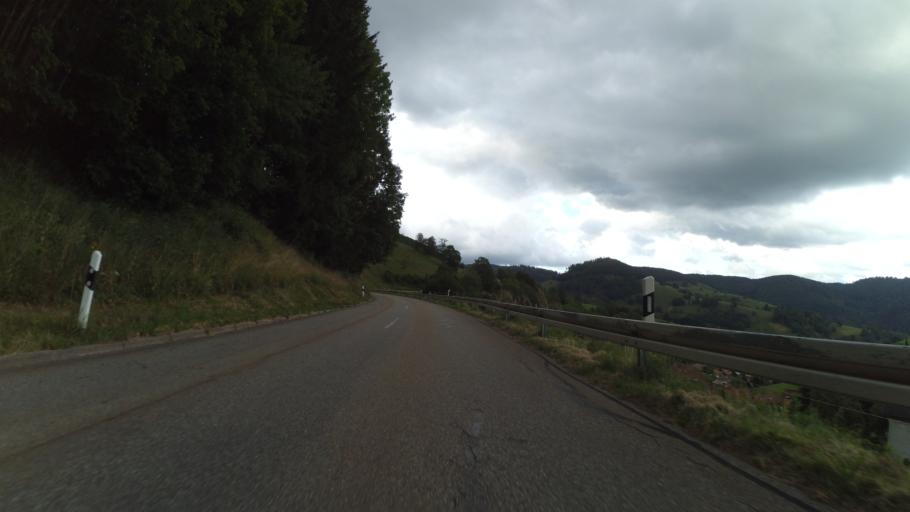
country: DE
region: Baden-Wuerttemberg
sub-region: Freiburg Region
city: Wieden
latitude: 47.8423
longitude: 7.8798
